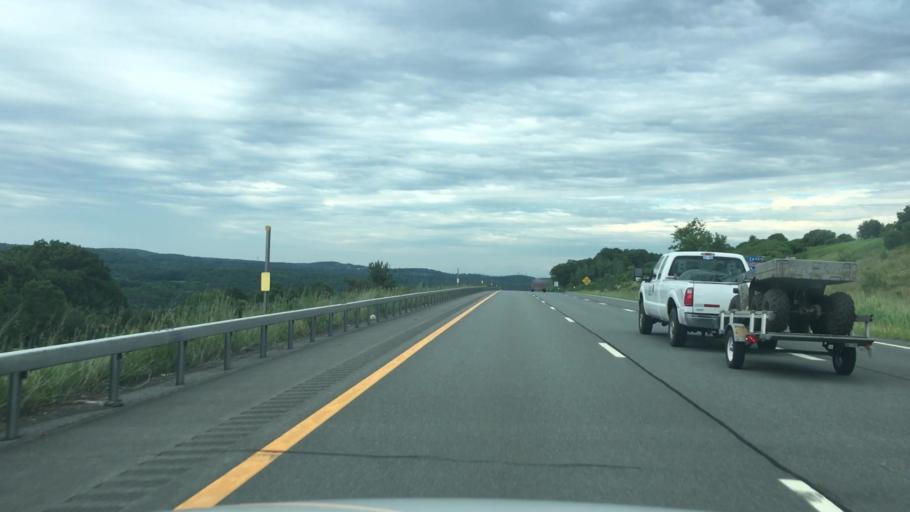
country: US
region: New York
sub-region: Albany County
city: Altamont
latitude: 42.7660
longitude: -74.1048
